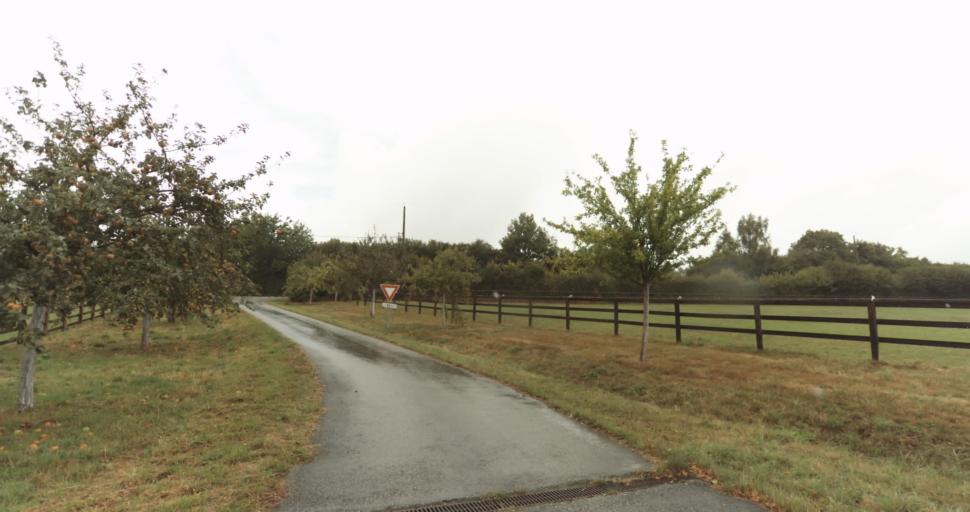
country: FR
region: Lower Normandy
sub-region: Departement de l'Orne
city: Sainte-Gauburge-Sainte-Colombe
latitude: 48.6977
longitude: 0.4207
